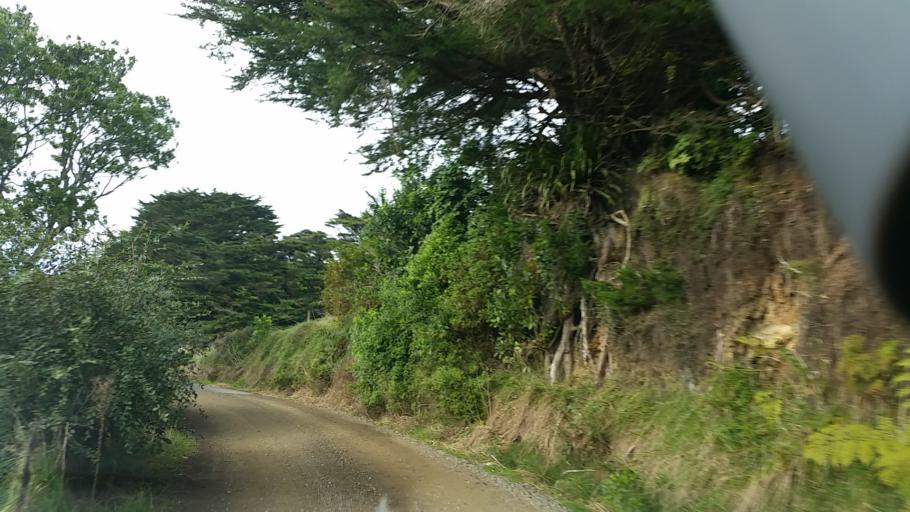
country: NZ
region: Taranaki
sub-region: New Plymouth District
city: Waitara
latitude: -39.0655
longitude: 174.3897
